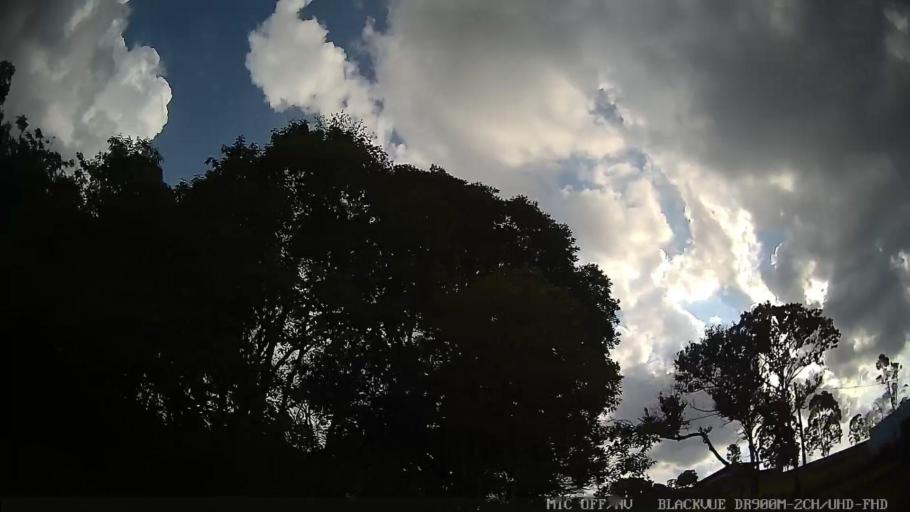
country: BR
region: Sao Paulo
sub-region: Braganca Paulista
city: Braganca Paulista
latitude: -22.9210
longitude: -46.4471
